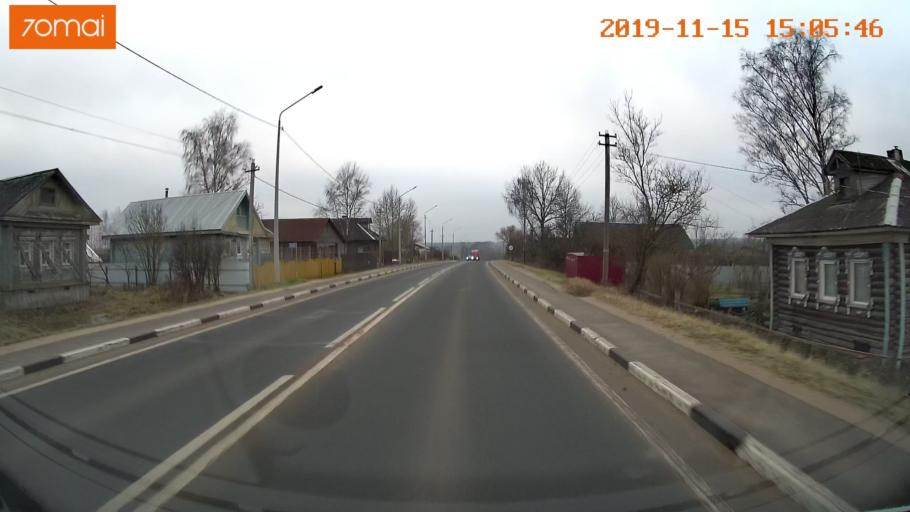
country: RU
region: Jaroslavl
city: Prechistoye
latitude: 58.3999
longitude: 40.3200
